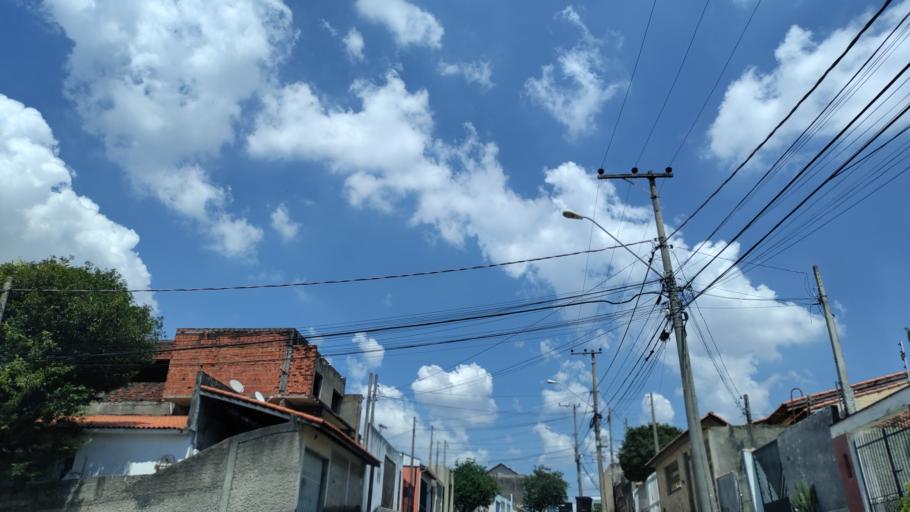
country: BR
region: Sao Paulo
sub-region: Sorocaba
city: Sorocaba
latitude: -23.4856
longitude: -47.4640
